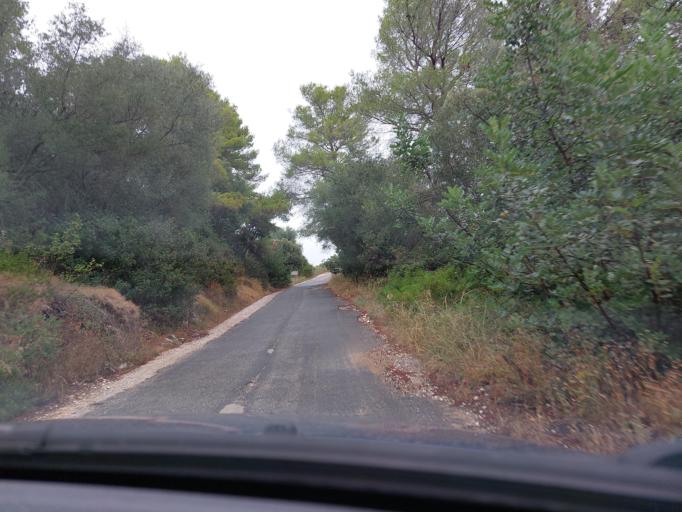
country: HR
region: Dubrovacko-Neretvanska
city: Smokvica
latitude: 42.7645
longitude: 16.9006
